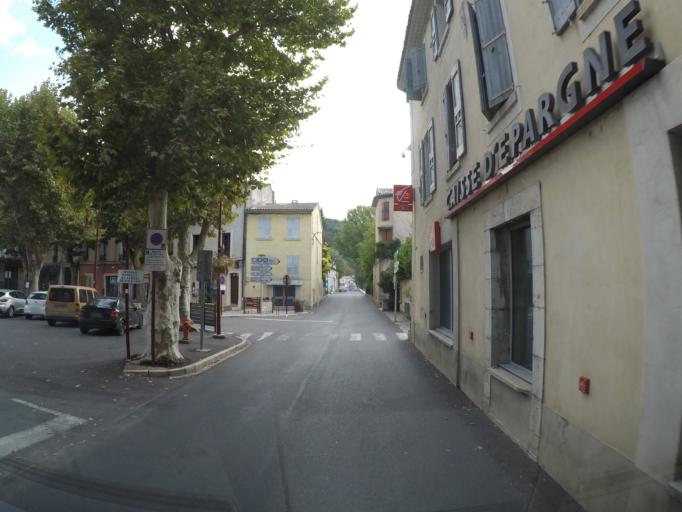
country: FR
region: Provence-Alpes-Cote d'Azur
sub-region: Departement des Alpes-de-Haute-Provence
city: Riez
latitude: 43.8182
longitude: 6.0905
